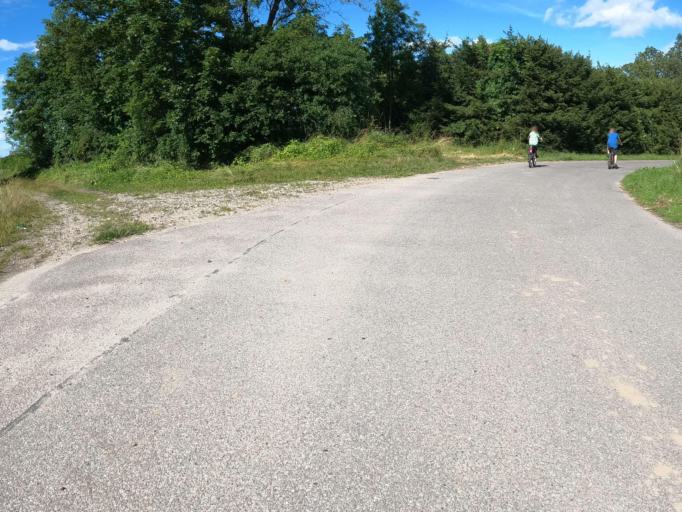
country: PL
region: West Pomeranian Voivodeship
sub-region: Powiat bialogardzki
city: Karlino
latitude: 53.9825
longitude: 15.8631
